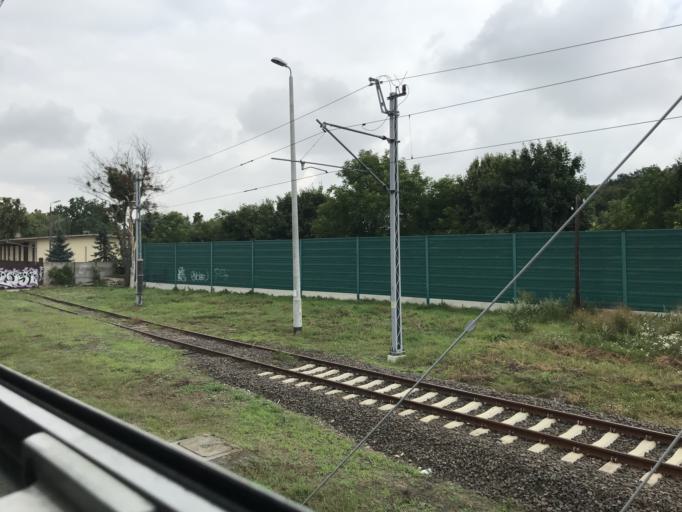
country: PL
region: Pomeranian Voivodeship
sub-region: Powiat malborski
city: Malbork
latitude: 54.0397
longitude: 19.0360
